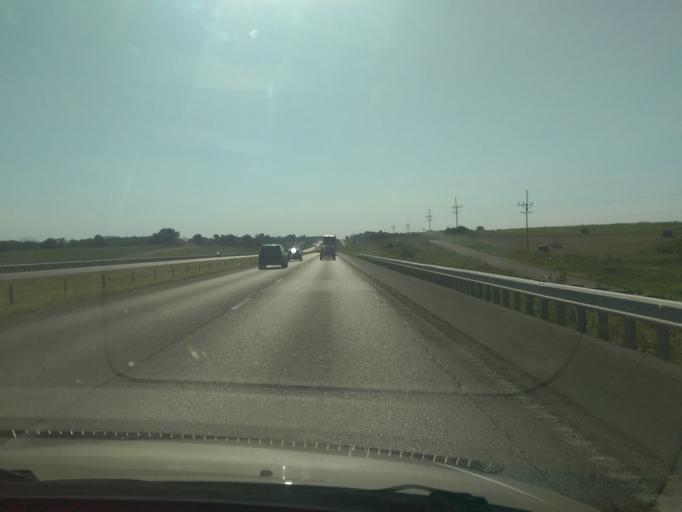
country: US
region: Missouri
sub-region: Lafayette County
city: Higginsville
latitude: 39.0020
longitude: -93.7769
